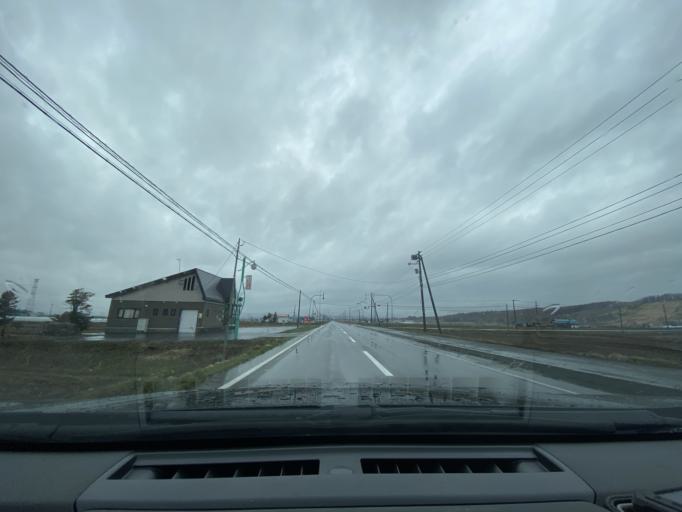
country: JP
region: Hokkaido
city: Fukagawa
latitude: 43.8146
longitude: 141.9740
